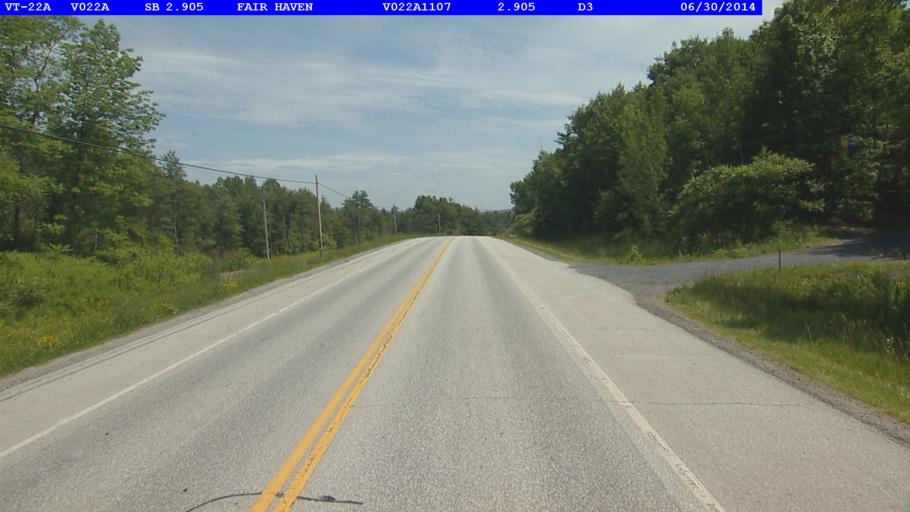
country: US
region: Vermont
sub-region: Rutland County
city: Fair Haven
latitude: 43.6104
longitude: -73.2834
